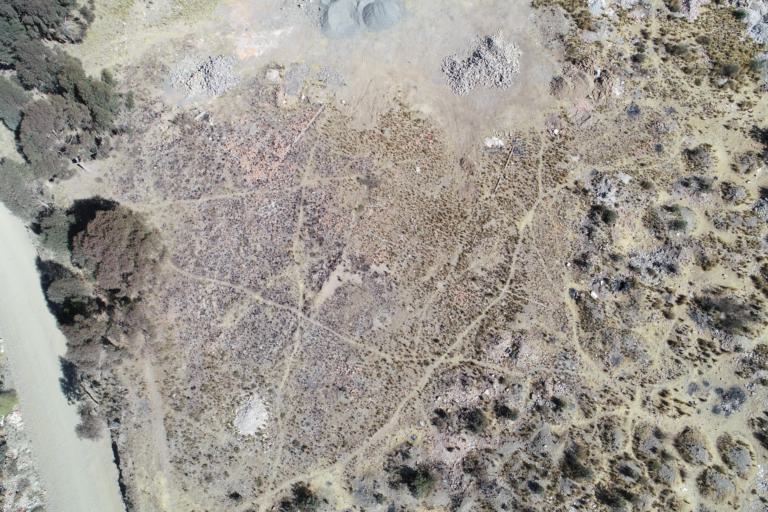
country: BO
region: La Paz
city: La Paz
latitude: -16.5413
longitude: -68.1527
